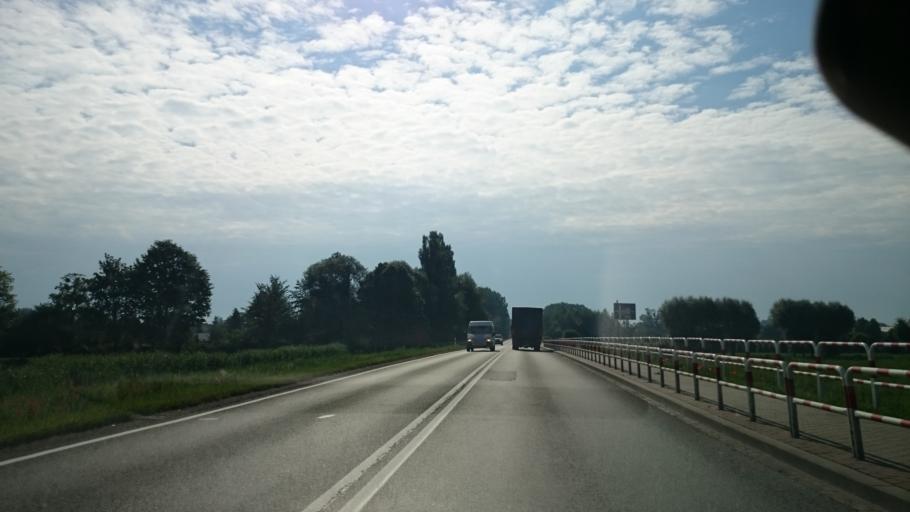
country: PL
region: Opole Voivodeship
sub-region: Powiat strzelecki
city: Strzelce Opolskie
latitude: 50.5063
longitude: 18.3164
